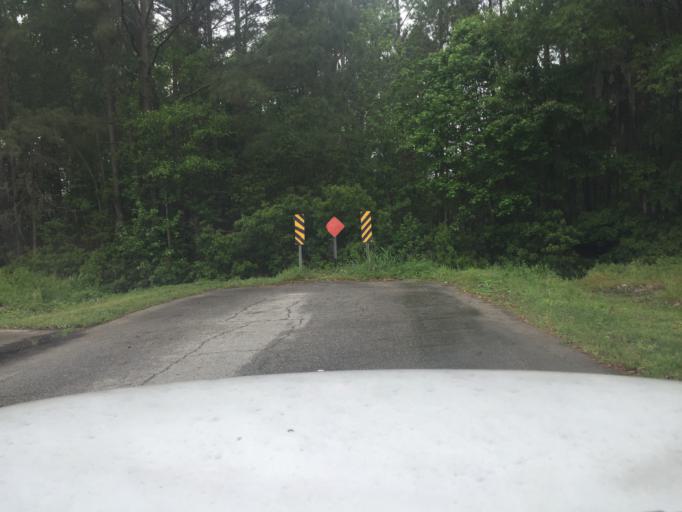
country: US
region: Georgia
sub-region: Chatham County
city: Georgetown
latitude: 32.0086
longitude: -81.2574
